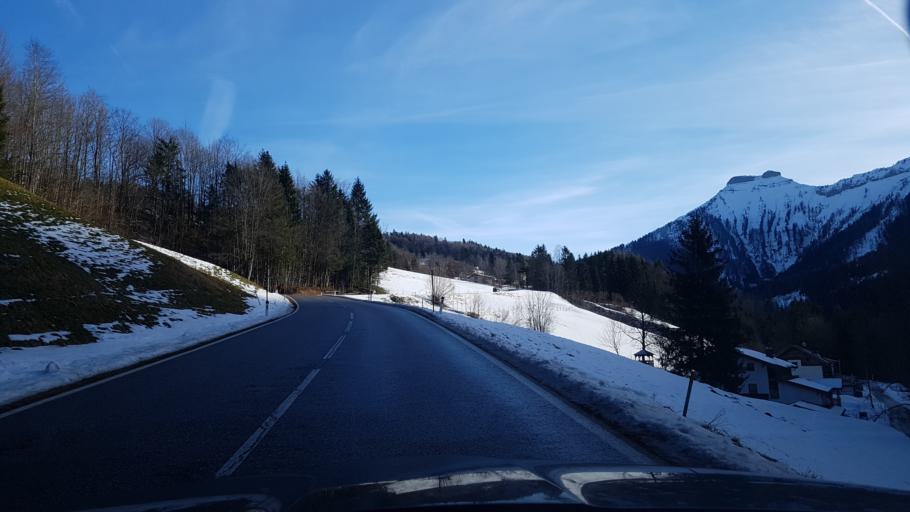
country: AT
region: Salzburg
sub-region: Politischer Bezirk Hallein
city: Krispl
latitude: 47.7088
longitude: 13.1989
